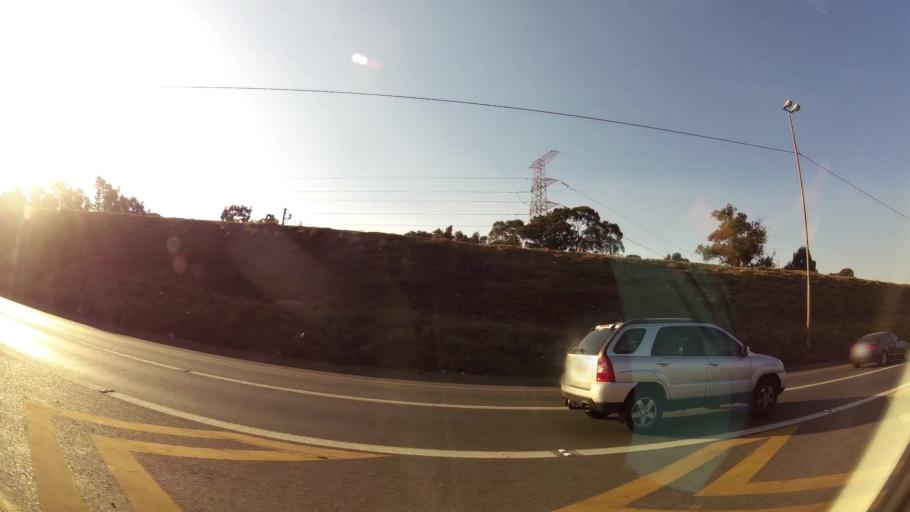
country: ZA
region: Gauteng
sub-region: Ekurhuleni Metropolitan Municipality
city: Germiston
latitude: -26.2105
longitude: 28.1274
